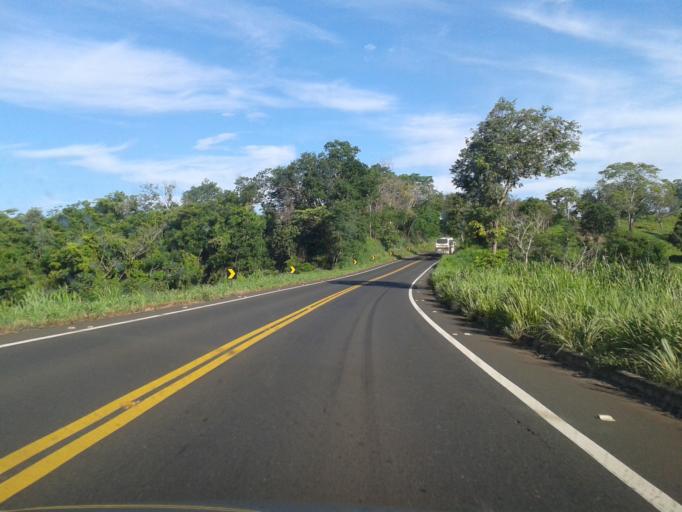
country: BR
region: Goias
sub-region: Caldas Novas
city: Caldas Novas
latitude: -18.1116
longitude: -48.6152
